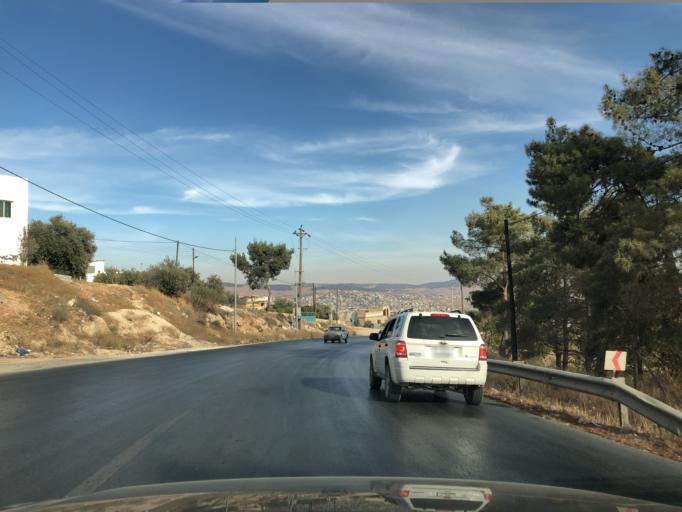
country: JO
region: Irbid
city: Al Kittah
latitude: 32.2808
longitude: 35.8657
